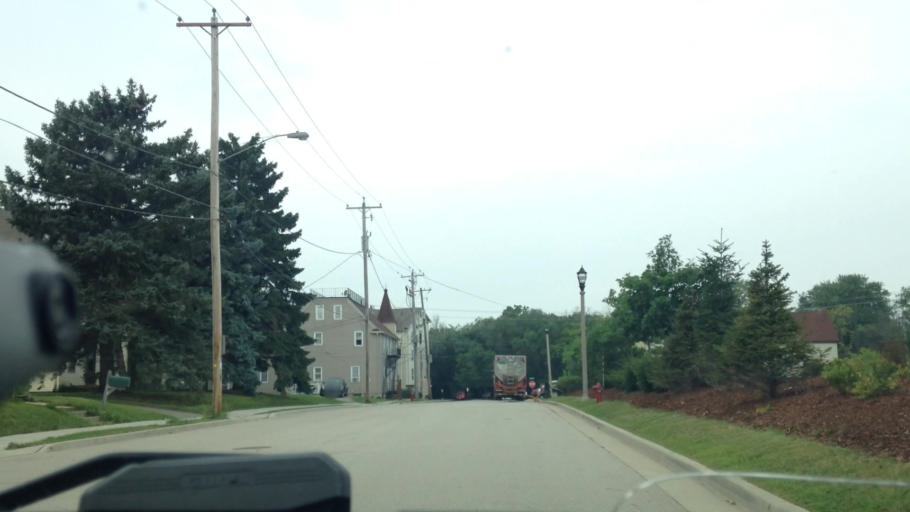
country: US
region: Wisconsin
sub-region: Waukesha County
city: Menomonee Falls
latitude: 43.1834
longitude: -88.1117
